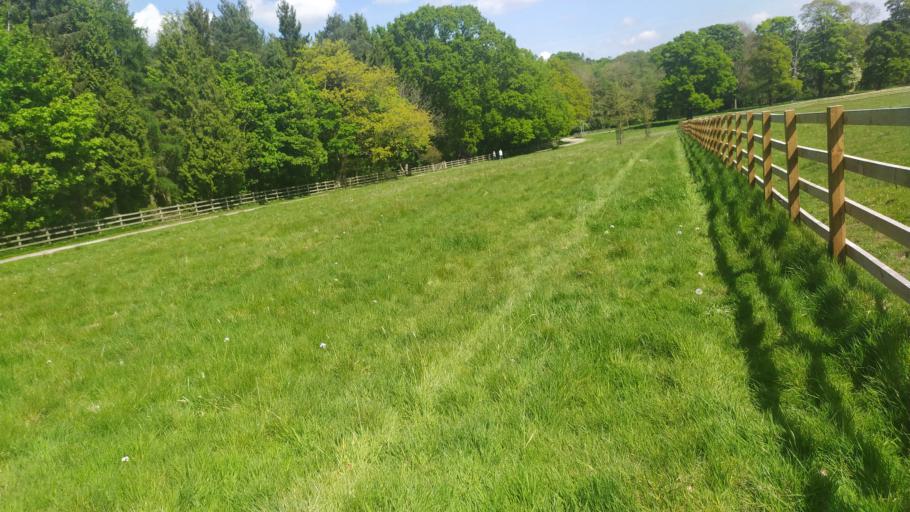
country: GB
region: England
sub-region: City and Borough of Leeds
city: Chapel Allerton
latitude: 53.8913
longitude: -1.5363
